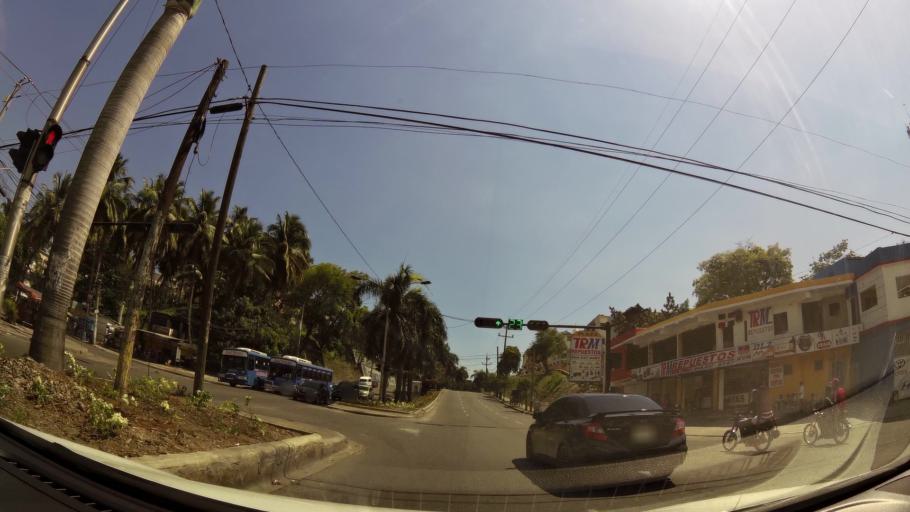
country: DO
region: Santo Domingo
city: Santo Domingo Oeste
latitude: 18.4735
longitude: -69.9945
